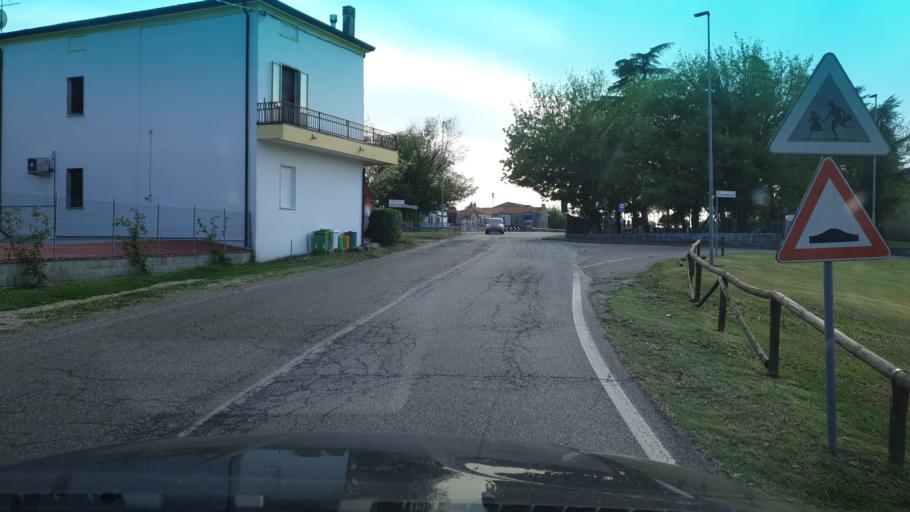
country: IT
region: Veneto
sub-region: Provincia di Rovigo
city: Castelguglielmo
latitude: 45.0265
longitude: 11.5394
